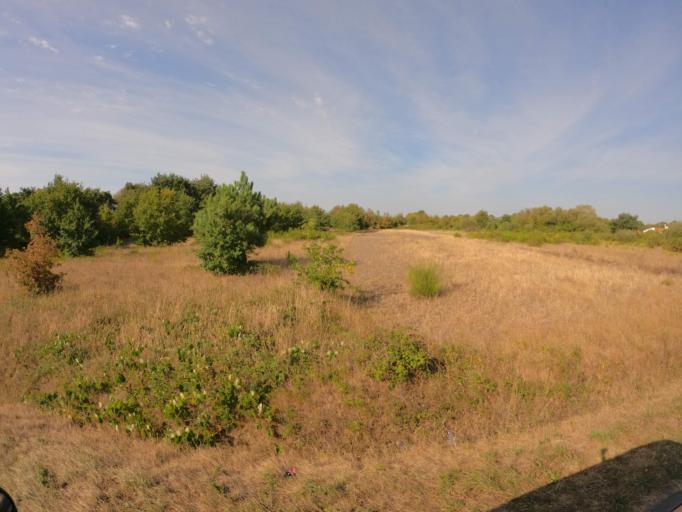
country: FR
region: Pays de la Loire
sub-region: Departement de la Vendee
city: Soullans
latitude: 46.8045
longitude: -1.9153
